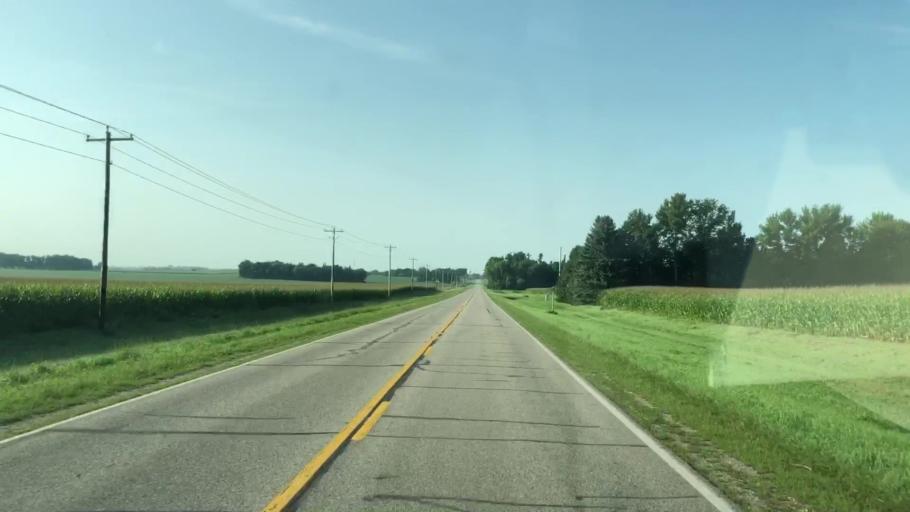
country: US
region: Iowa
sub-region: Lyon County
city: George
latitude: 43.3710
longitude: -95.9982
